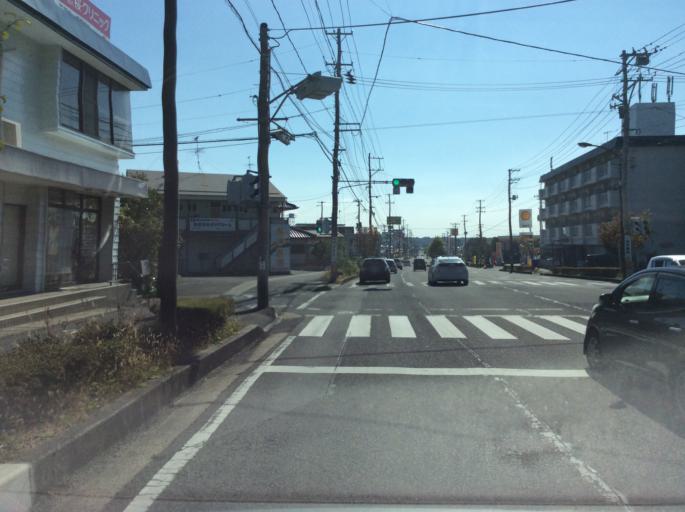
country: JP
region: Fukushima
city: Koriyama
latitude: 37.3799
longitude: 140.3587
